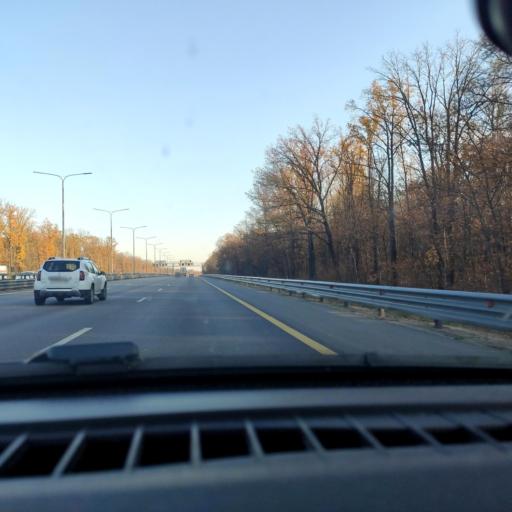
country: RU
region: Voronezj
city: Podgornoye
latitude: 51.8353
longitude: 39.2287
